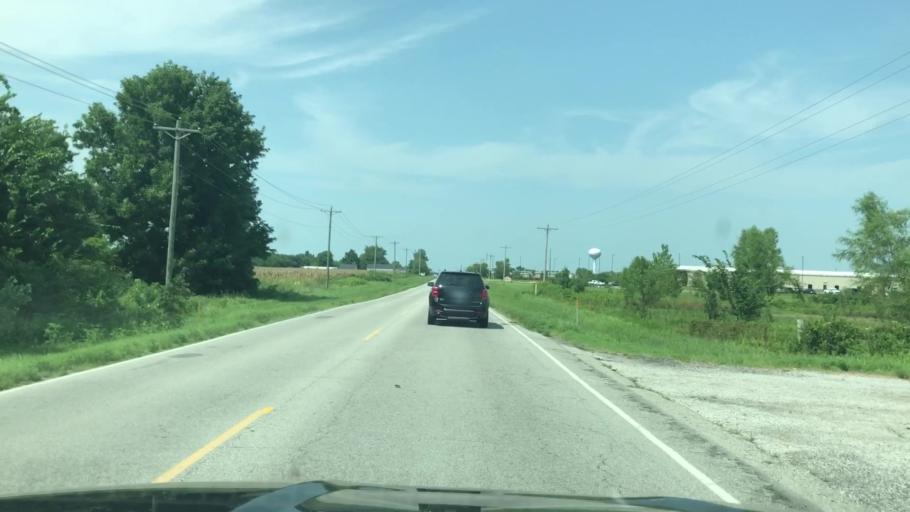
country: US
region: Oklahoma
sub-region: Ottawa County
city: Commerce
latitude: 36.9037
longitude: -94.8419
